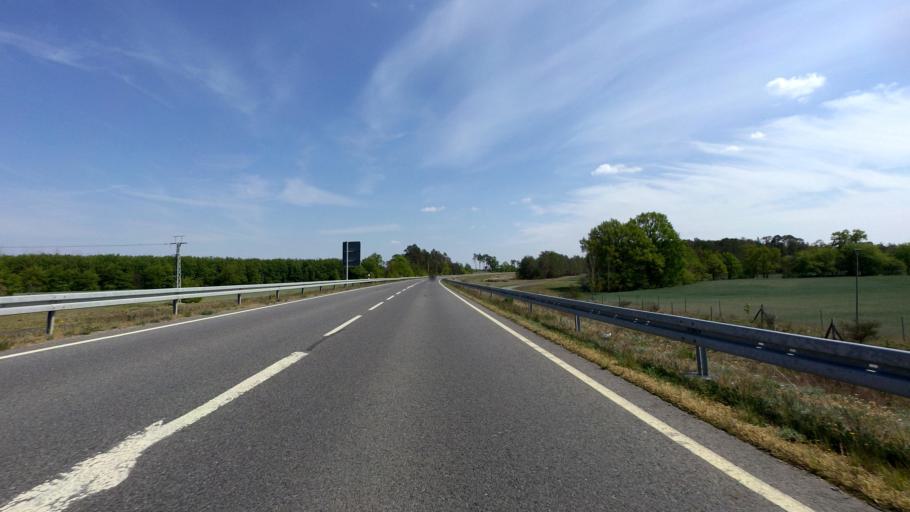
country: DE
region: Brandenburg
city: Cottbus
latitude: 51.7840
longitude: 14.3809
